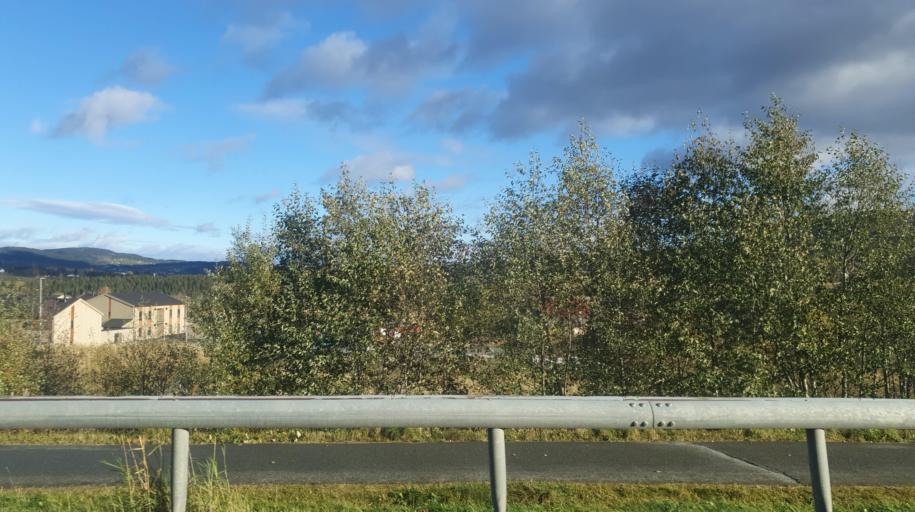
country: NO
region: Sor-Trondelag
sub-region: Klaebu
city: Klaebu
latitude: 63.3021
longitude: 10.4684
